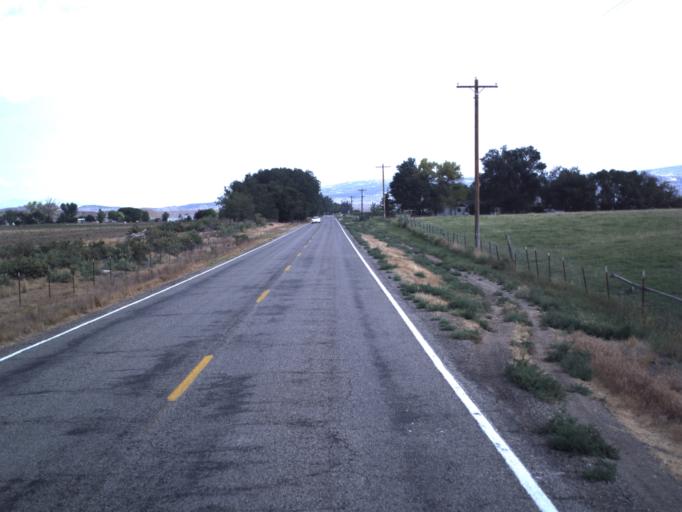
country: US
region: Utah
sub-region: Uintah County
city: Naples
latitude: 40.3931
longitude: -109.3460
